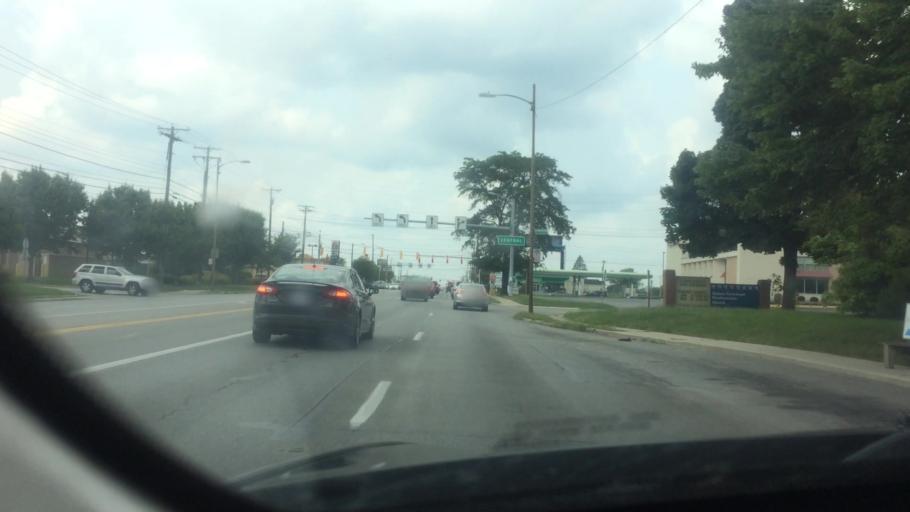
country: US
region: Ohio
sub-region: Lucas County
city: Ottawa Hills
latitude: 41.6759
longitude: -83.6225
